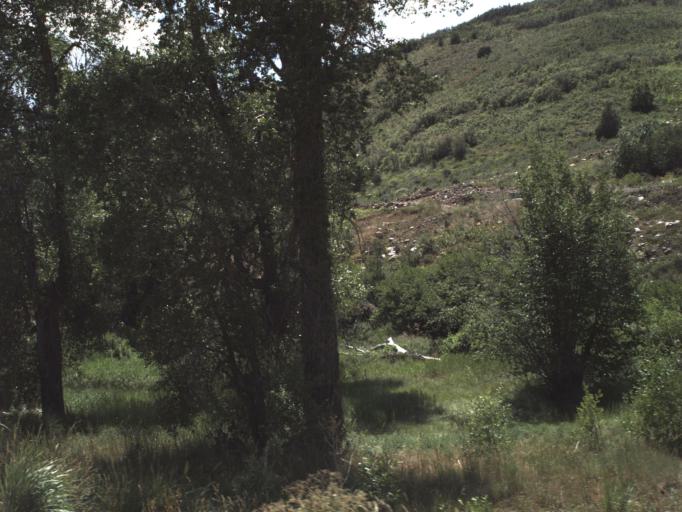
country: US
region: Utah
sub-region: Weber County
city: Wolf Creek
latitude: 41.3673
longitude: -111.5906
